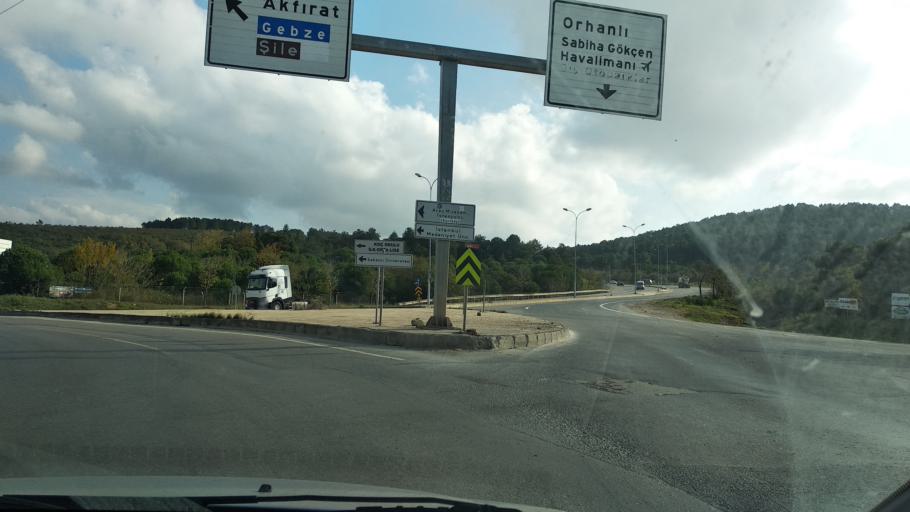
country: TR
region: Istanbul
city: Sultanbeyli
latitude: 40.9306
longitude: 29.3347
